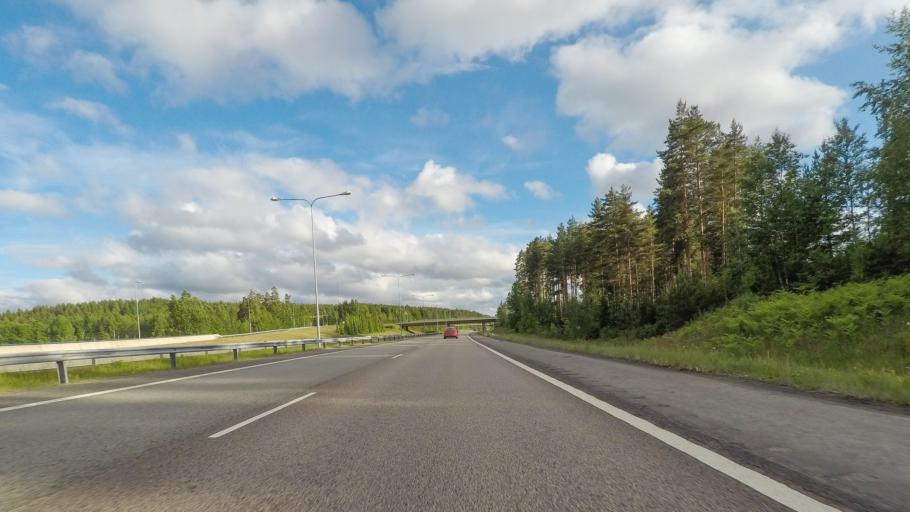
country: FI
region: Paijanne Tavastia
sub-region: Lahti
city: Heinola
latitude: 61.1955
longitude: 26.0026
